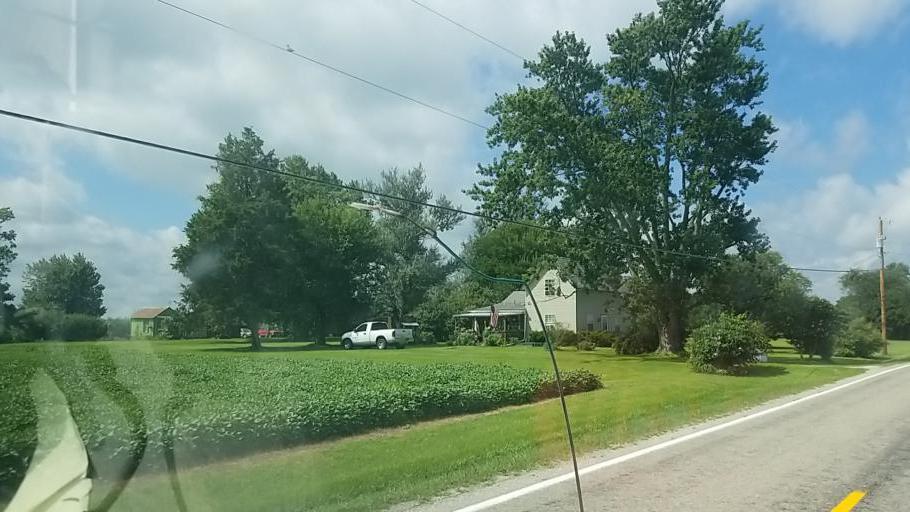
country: US
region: Ohio
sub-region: Madison County
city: Bethel
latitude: 39.7318
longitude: -83.4183
